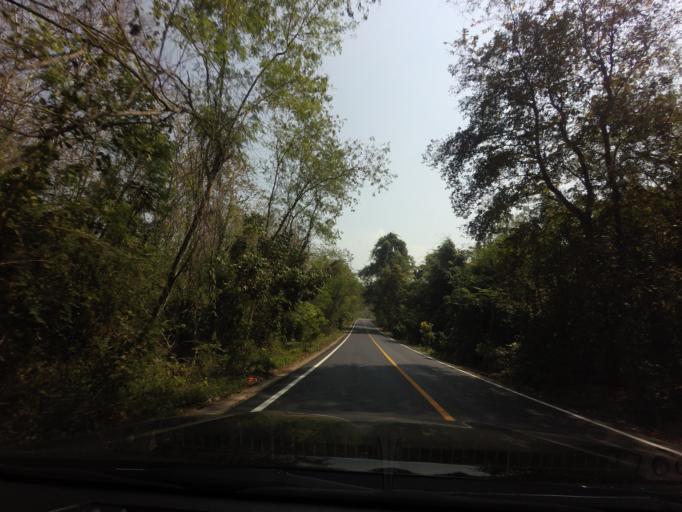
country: TH
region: Kanchanaburi
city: Thong Pha Phum
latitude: 14.7801
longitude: 98.5946
